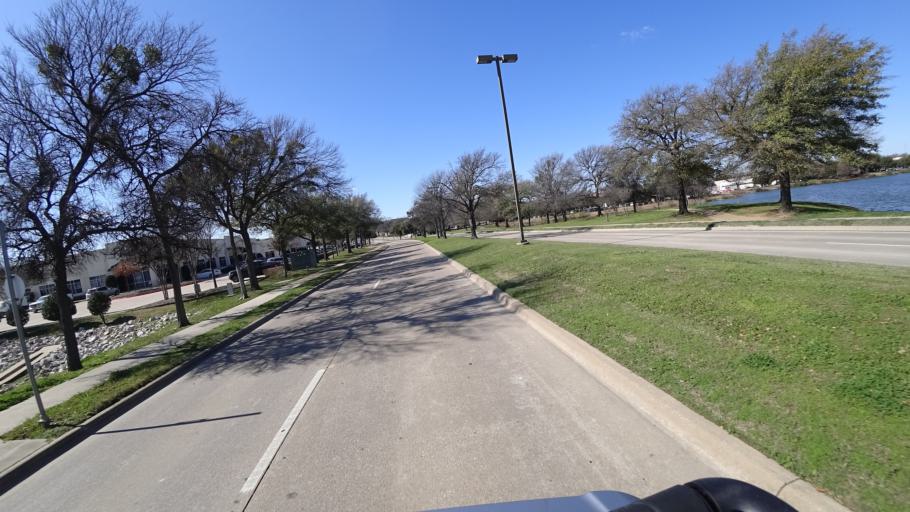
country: US
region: Texas
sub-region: Denton County
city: Lewisville
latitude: 33.0209
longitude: -96.9756
